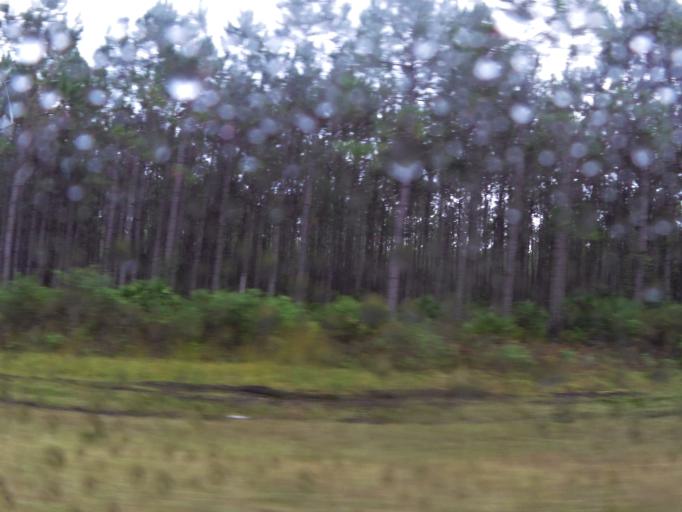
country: US
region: Florida
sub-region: Baker County
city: Macclenny
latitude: 30.4164
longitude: -82.1029
